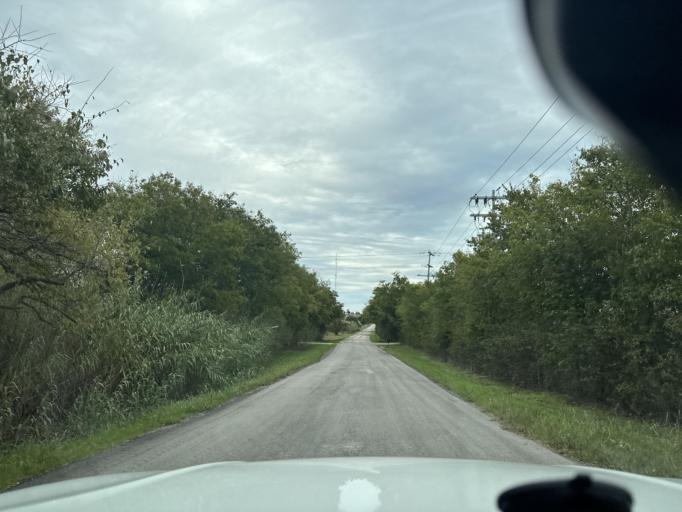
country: US
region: Texas
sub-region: Burleson County
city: Somerville
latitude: 30.1602
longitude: -96.6436
